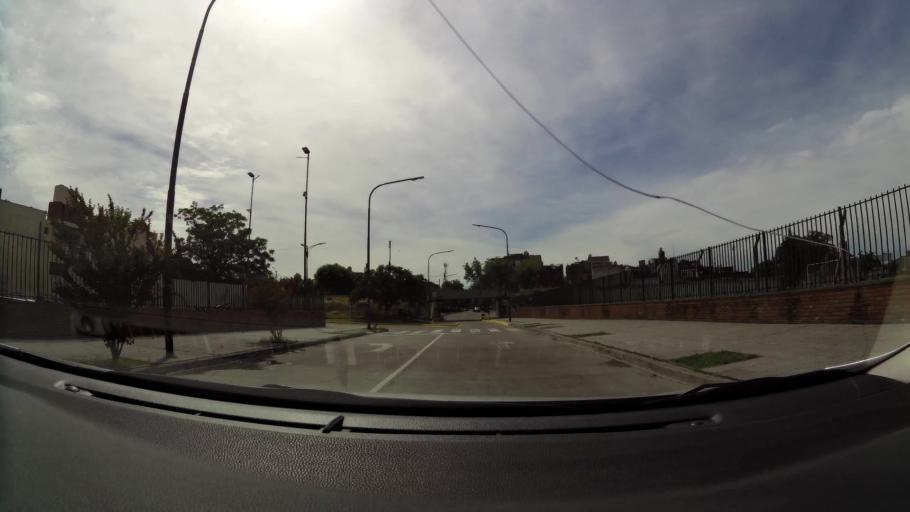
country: AR
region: Buenos Aires F.D.
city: Villa Lugano
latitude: -34.6561
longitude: -58.4306
